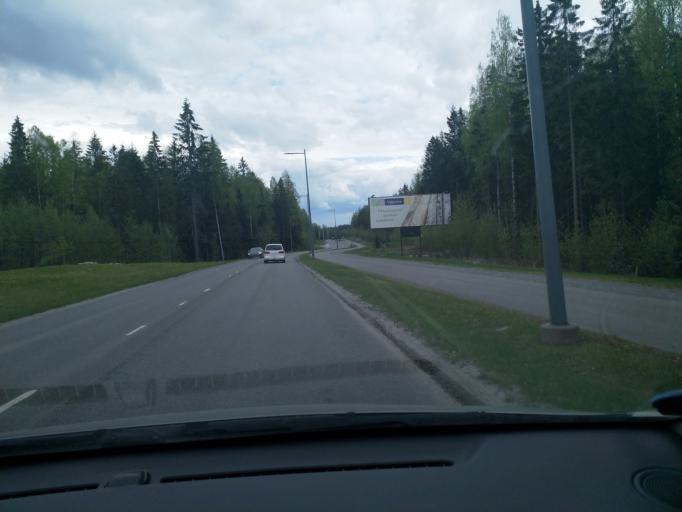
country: FI
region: Pirkanmaa
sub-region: Tampere
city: Tampere
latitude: 61.4546
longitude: 23.7959
